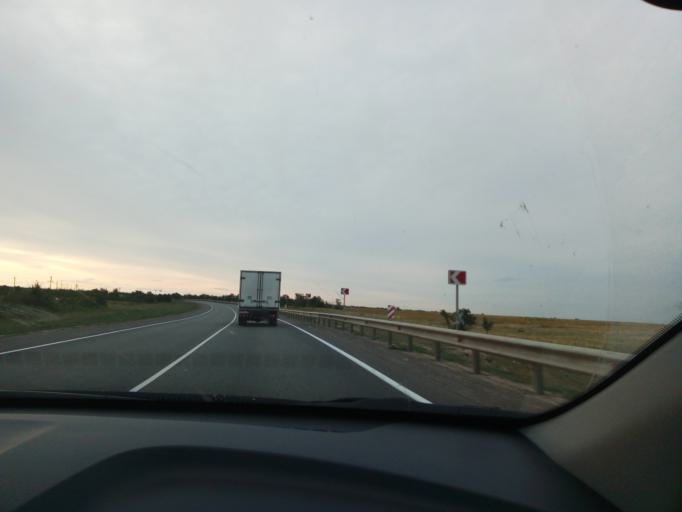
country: RU
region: Volgograd
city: Primorsk
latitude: 49.2196
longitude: 44.9070
